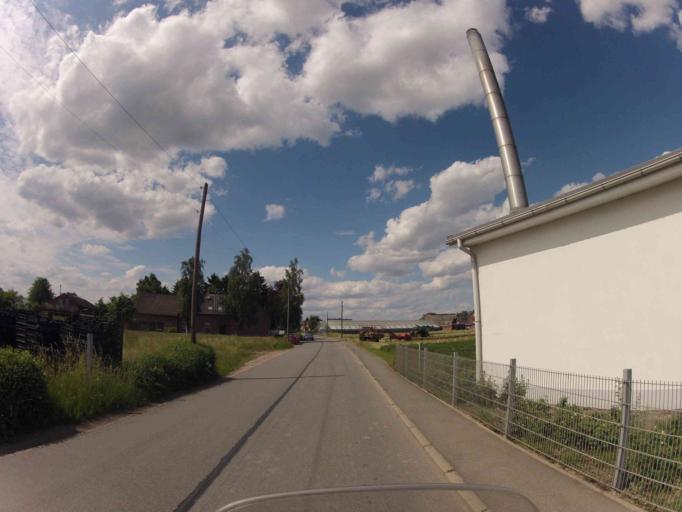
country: DE
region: Hamburg
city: Bergedorf
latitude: 53.4276
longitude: 10.1989
